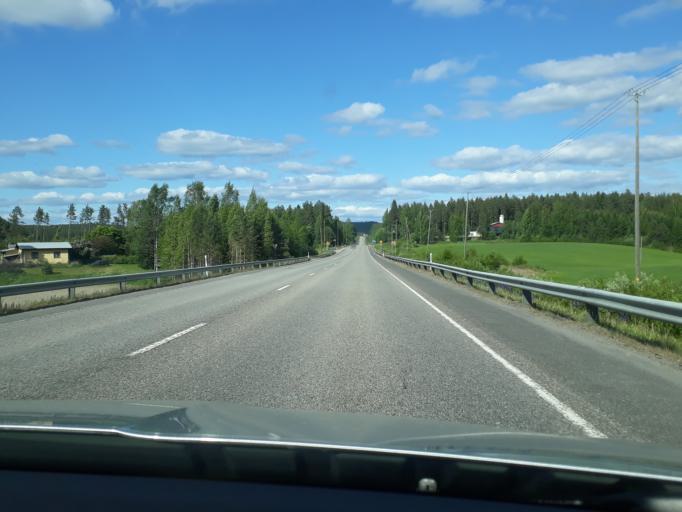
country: FI
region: Central Finland
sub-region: AEaenekoski
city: AEaenekoski
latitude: 62.6532
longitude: 25.7210
